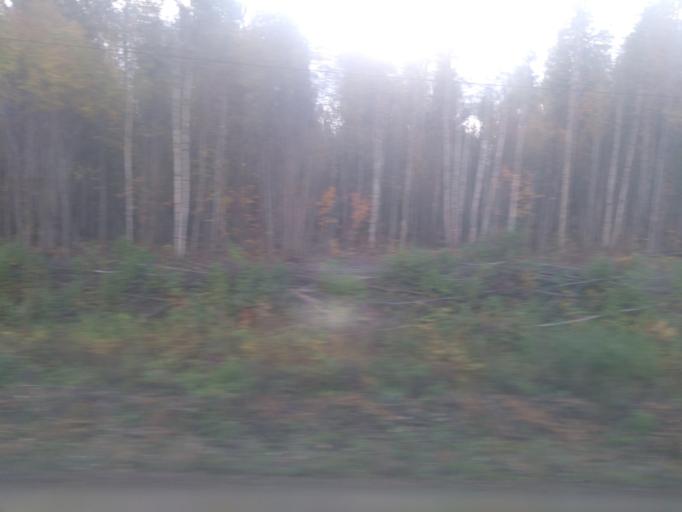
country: RU
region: Udmurtiya
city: Mozhga
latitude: 56.4264
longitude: 52.0534
